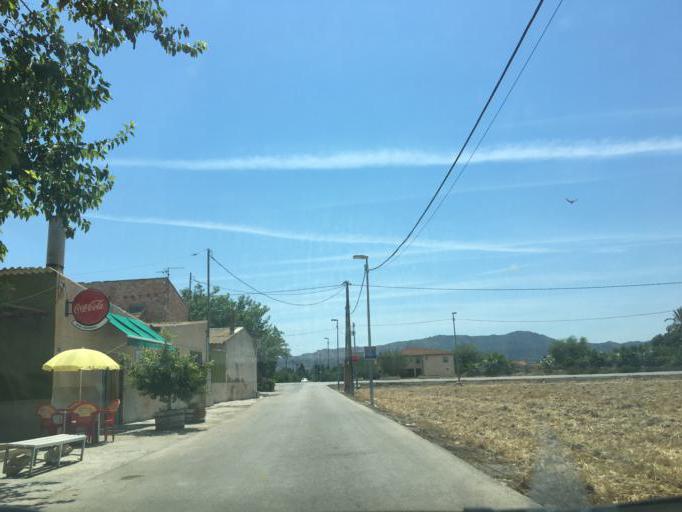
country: ES
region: Murcia
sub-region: Murcia
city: Santomera
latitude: 38.0249
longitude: -1.0597
